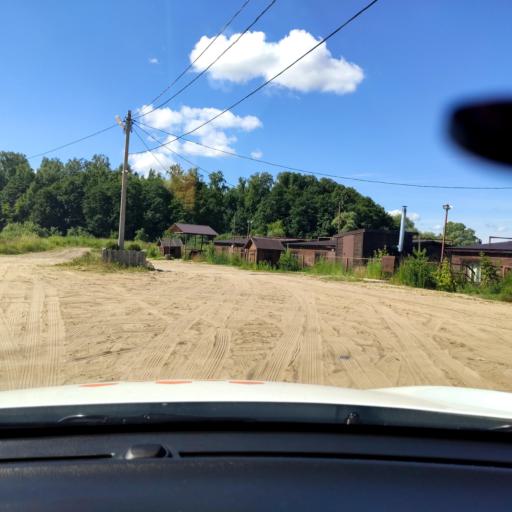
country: RU
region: Tatarstan
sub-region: Gorod Kazan'
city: Kazan
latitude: 55.8332
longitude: 49.1824
